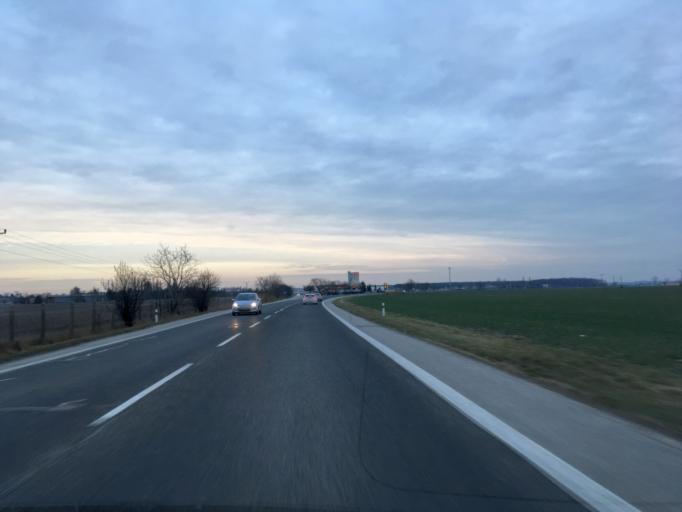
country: SK
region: Trnavsky
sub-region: Okres Dunajska Streda
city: Velky Meder
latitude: 47.8727
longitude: 17.7570
